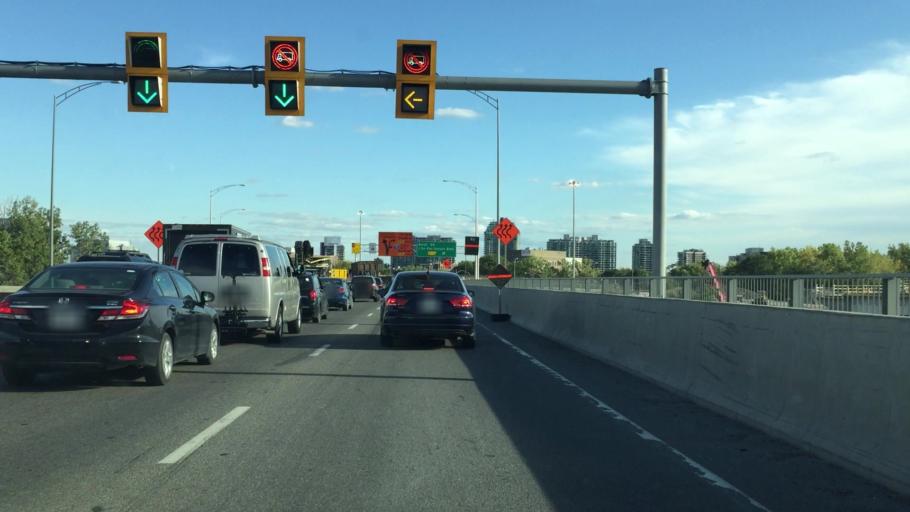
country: CA
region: Quebec
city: Westmount
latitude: 45.4725
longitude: -73.5475
